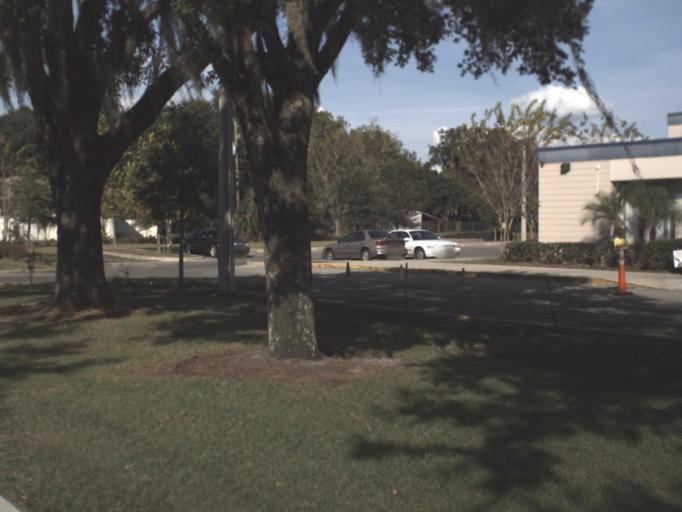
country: US
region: Florida
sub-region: Seminole County
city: Sanford
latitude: 28.8034
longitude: -81.2889
